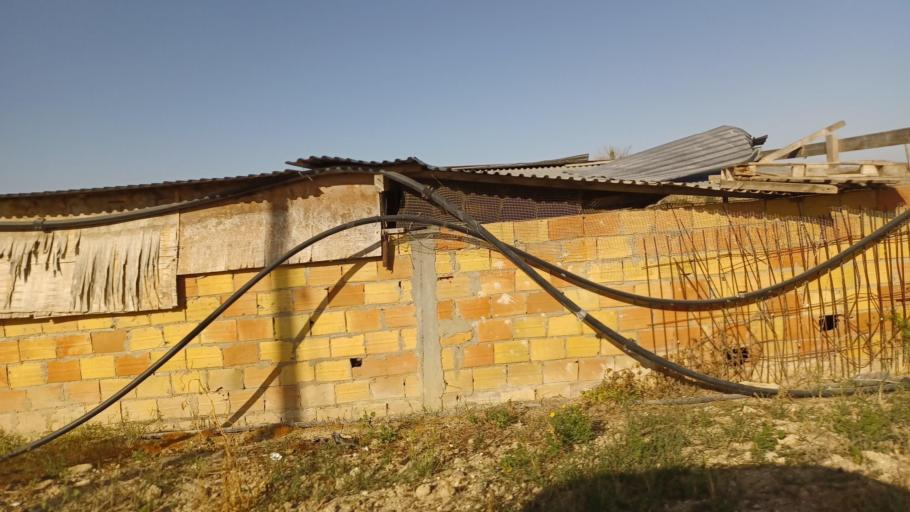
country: CY
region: Lefkosia
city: Mammari
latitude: 35.1657
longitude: 33.2493
